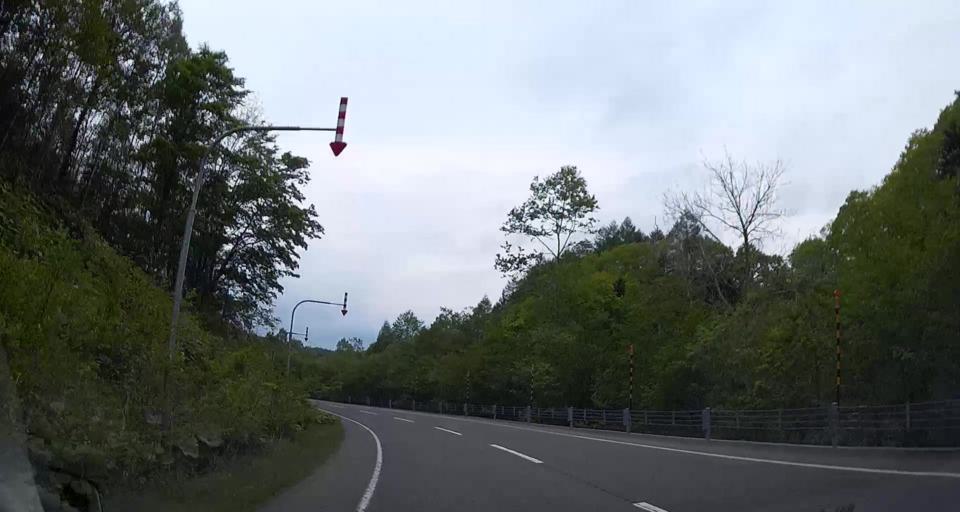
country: JP
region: Hokkaido
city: Shiraoi
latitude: 42.6751
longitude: 141.1121
